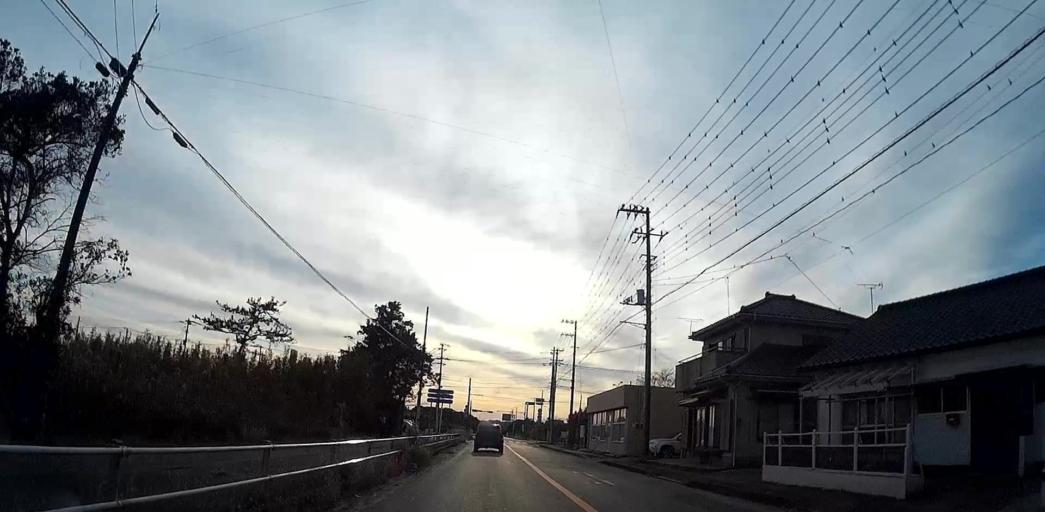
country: JP
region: Chiba
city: Hasaki
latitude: 35.7881
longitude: 140.7654
